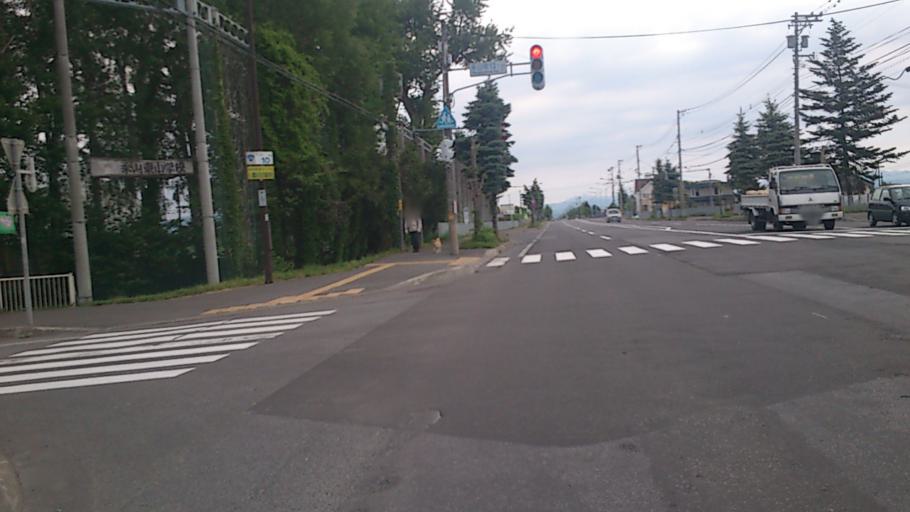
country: JP
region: Hokkaido
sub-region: Asahikawa-shi
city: Asahikawa
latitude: 43.8195
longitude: 142.4483
